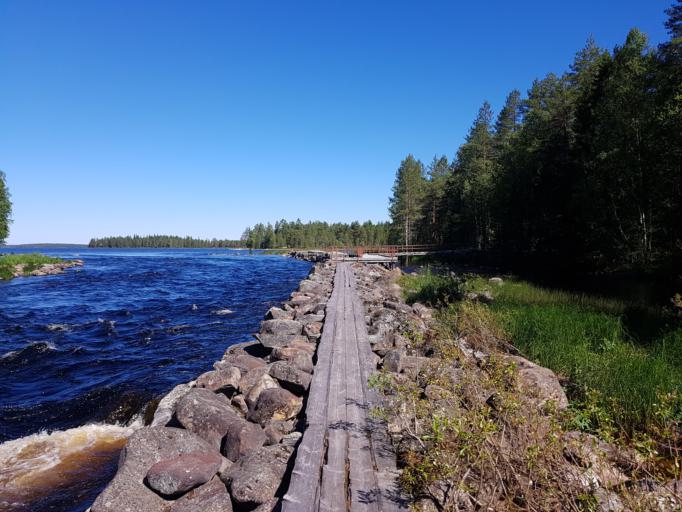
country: FI
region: Kainuu
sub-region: Kehys-Kainuu
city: Kuhmo
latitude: 64.1926
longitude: 29.5910
